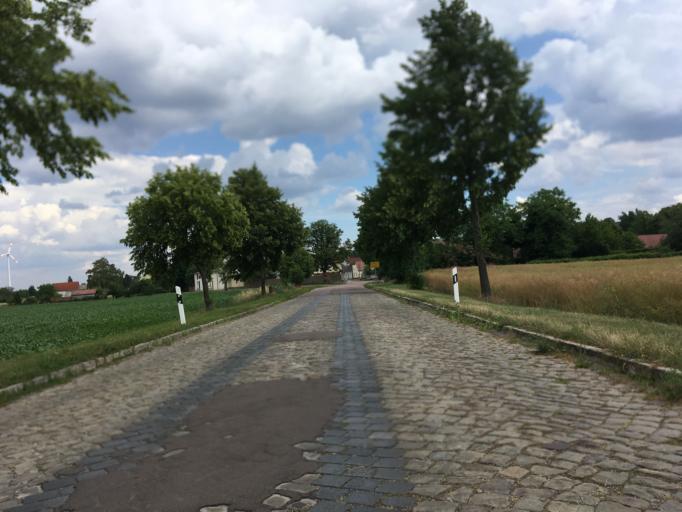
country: DE
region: Saxony-Anhalt
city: Baalberge
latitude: 51.7770
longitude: 11.8200
